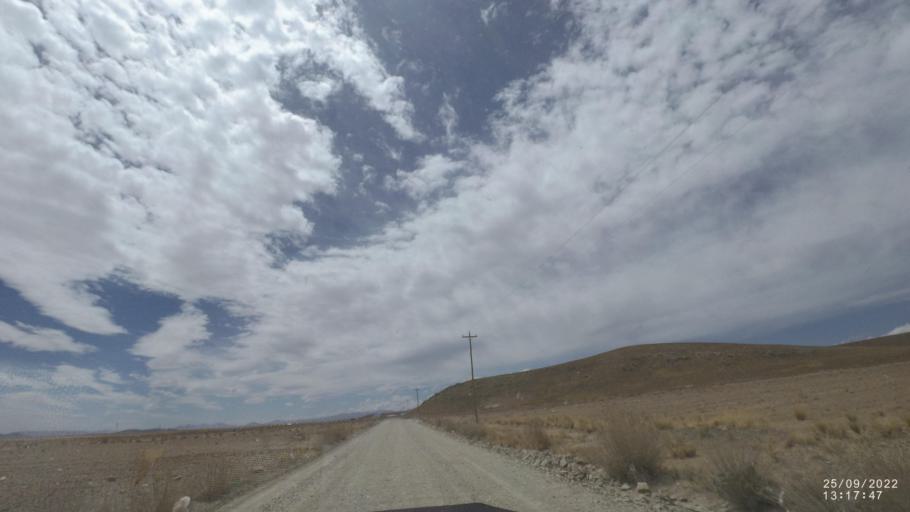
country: BO
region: Oruro
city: Oruro
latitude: -17.9053
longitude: -67.0443
